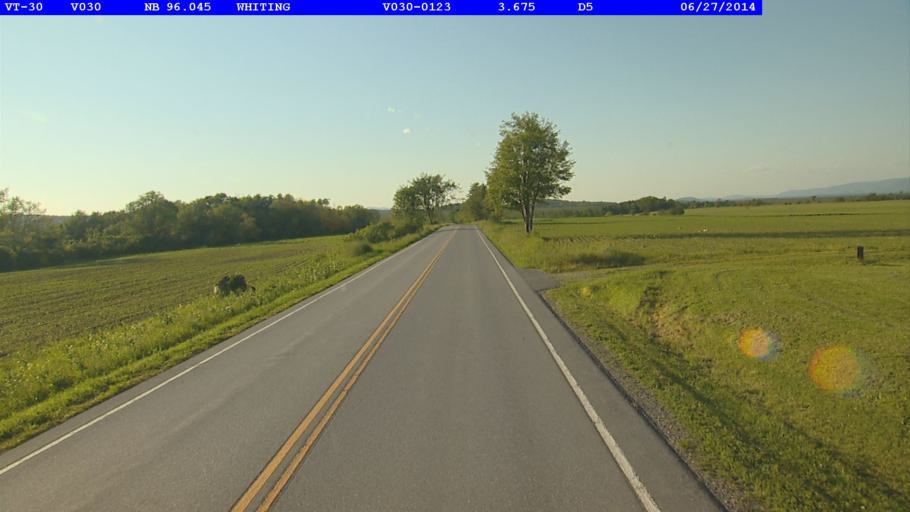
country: US
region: Vermont
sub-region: Addison County
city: Middlebury (village)
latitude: 43.8904
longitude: -73.2020
